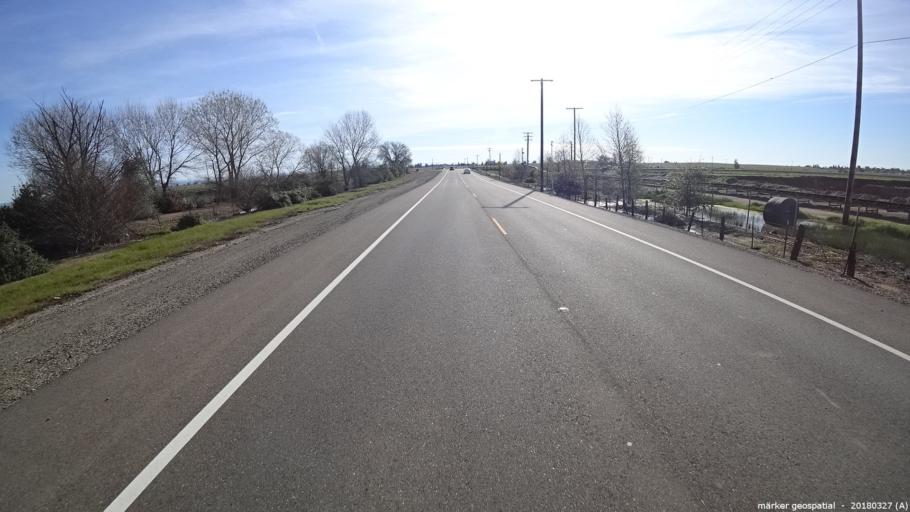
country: US
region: California
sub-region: Sacramento County
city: Wilton
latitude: 38.4967
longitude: -121.2463
